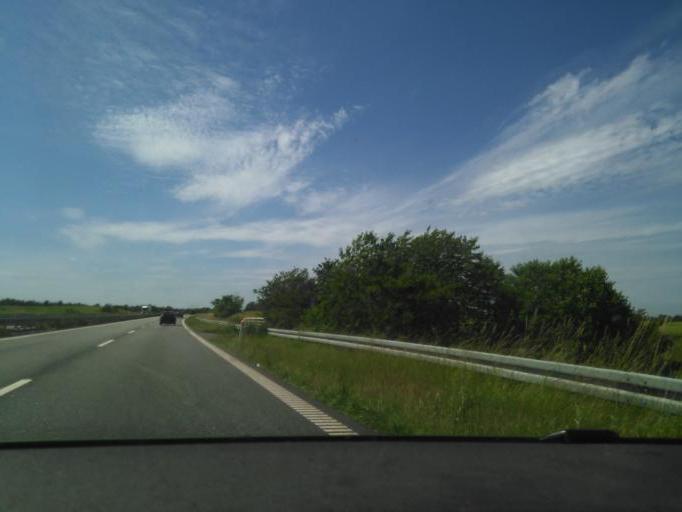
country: DK
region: Zealand
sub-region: Holbaek Kommune
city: Vipperod
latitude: 55.6479
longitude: 11.7235
